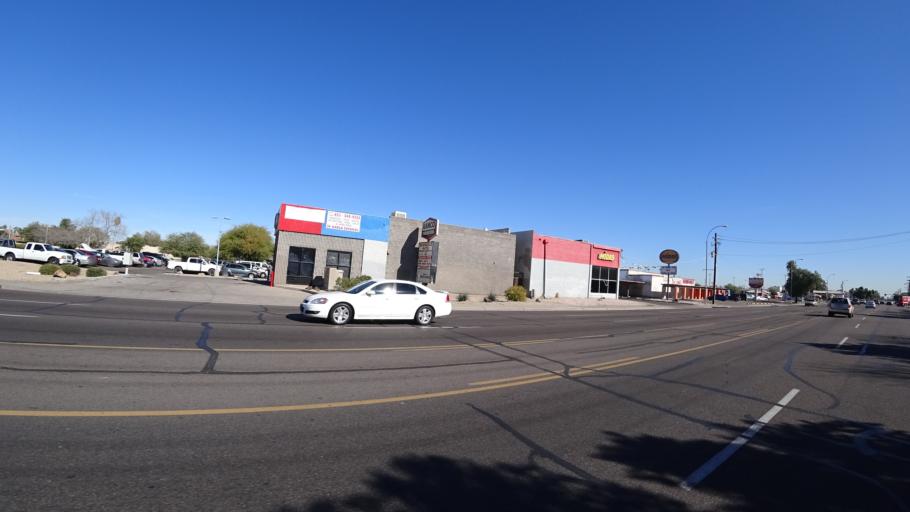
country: US
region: Arizona
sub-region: Maricopa County
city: Glendale
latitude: 33.4947
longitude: -112.2065
